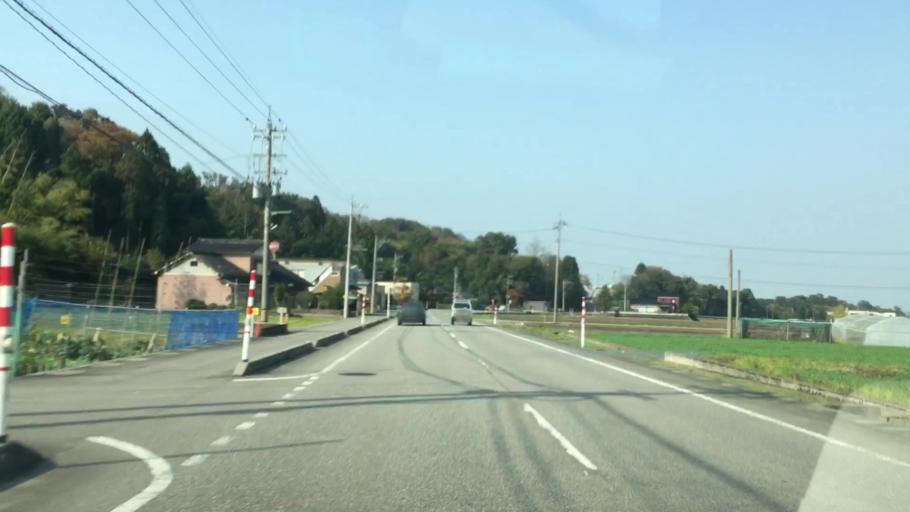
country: JP
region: Toyama
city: Toyama-shi
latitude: 36.6014
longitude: 137.2460
